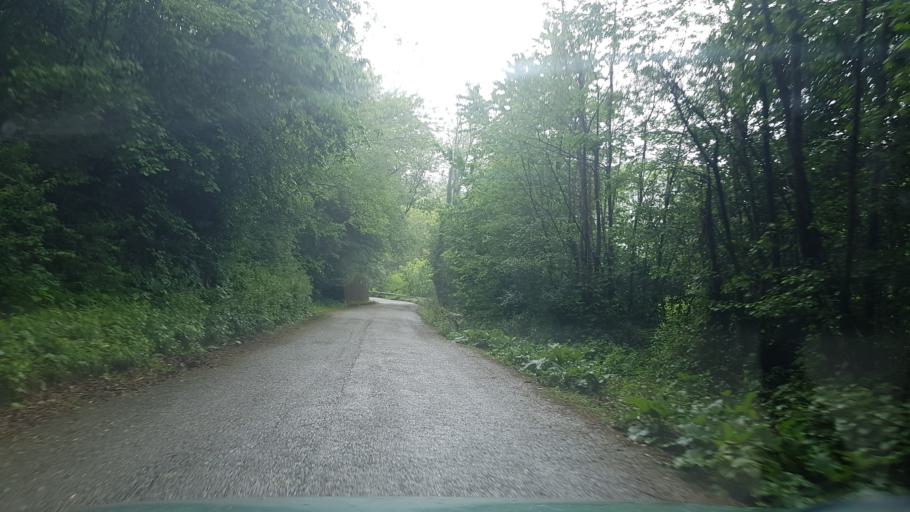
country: IT
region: Friuli Venezia Giulia
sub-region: Provincia di Gorizia
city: San Floriano del Collio
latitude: 45.9565
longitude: 13.5986
